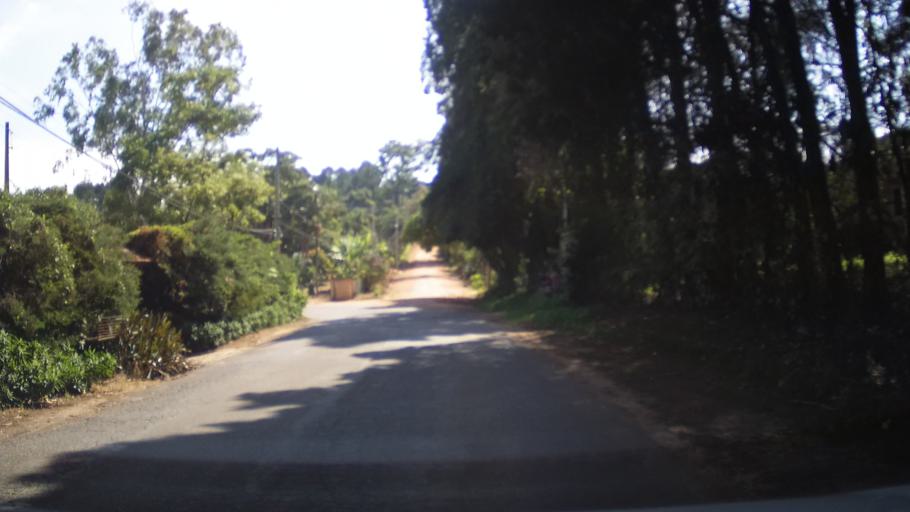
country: BR
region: Sao Paulo
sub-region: Itupeva
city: Itupeva
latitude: -23.2120
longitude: -47.0679
